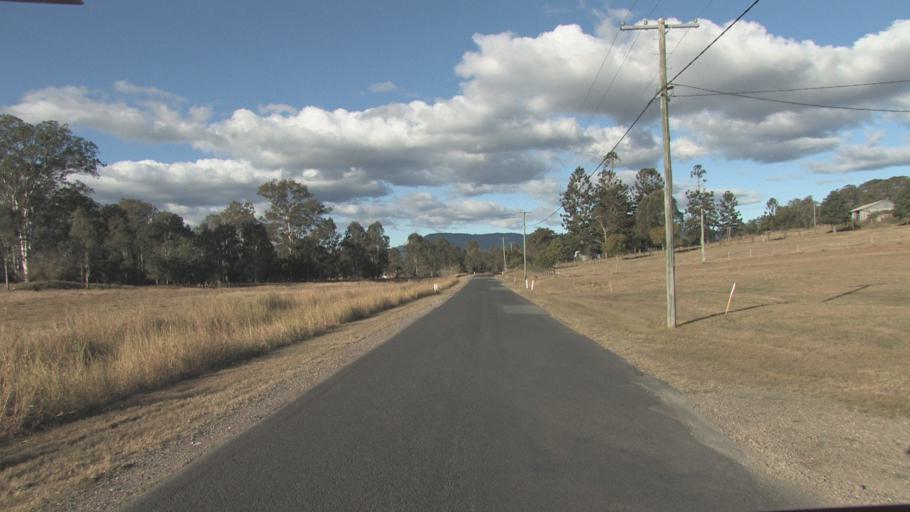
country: AU
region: Queensland
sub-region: Logan
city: Cedar Vale
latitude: -27.9286
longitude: 153.0765
